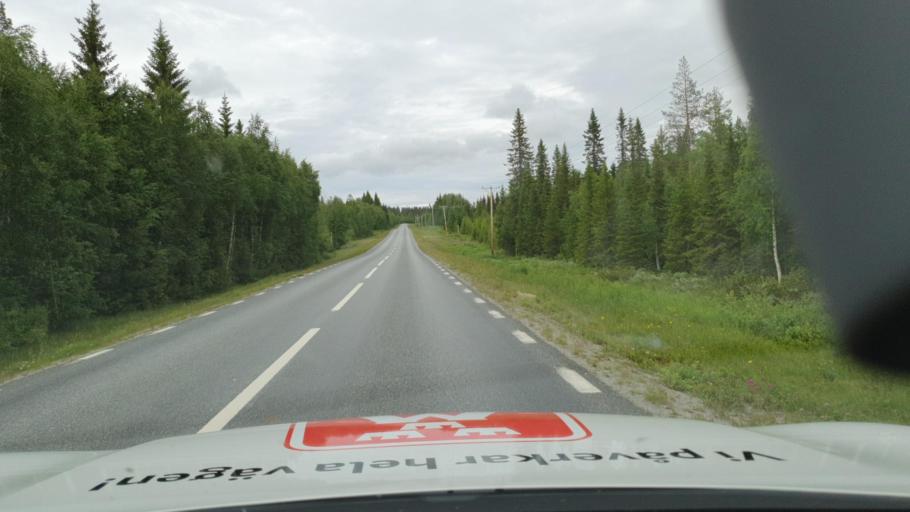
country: SE
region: Vaesterbotten
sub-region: Lycksele Kommun
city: Soderfors
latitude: 64.3759
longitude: 17.9774
